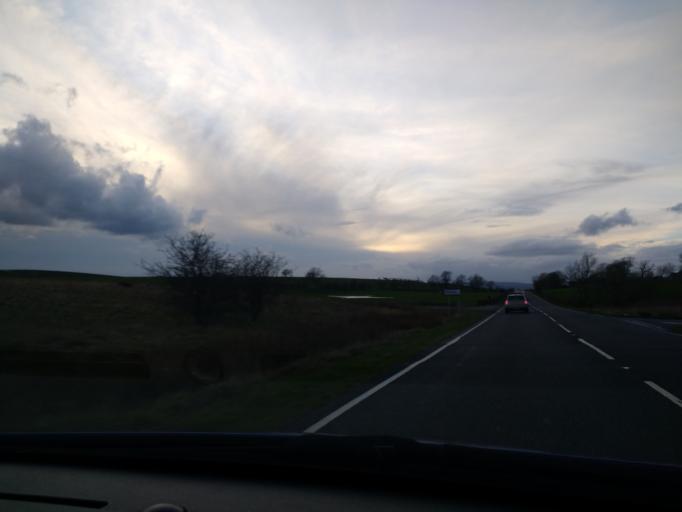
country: GB
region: England
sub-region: North Yorkshire
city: Ingleton
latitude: 54.1283
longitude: -2.4435
